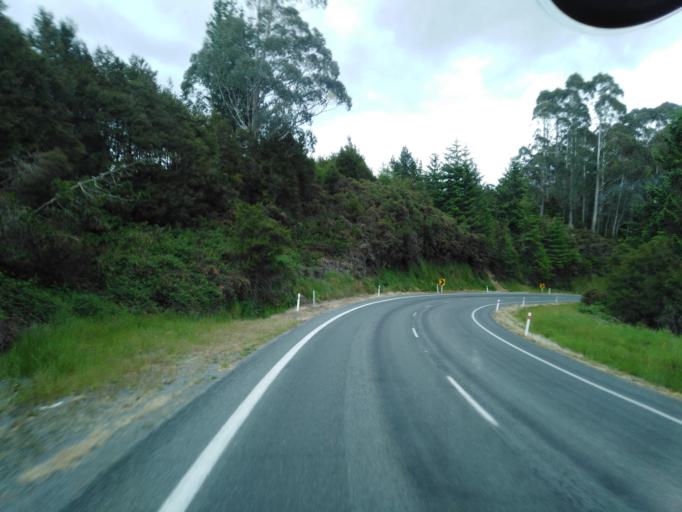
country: NZ
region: Tasman
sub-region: Tasman District
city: Wakefield
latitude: -41.6307
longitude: 172.7032
